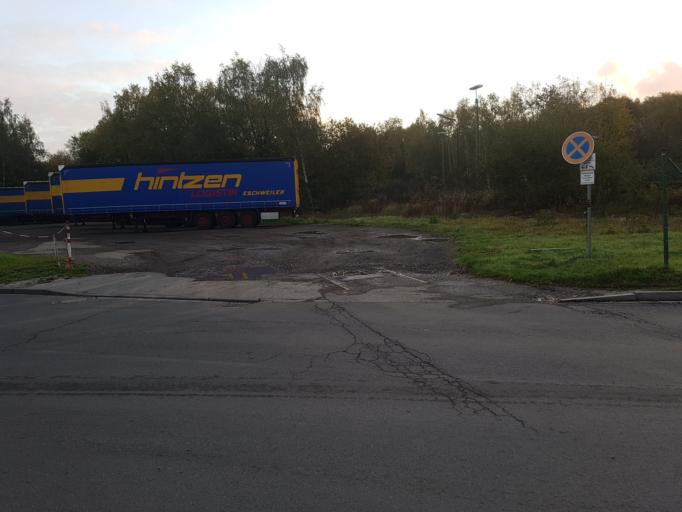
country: DE
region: North Rhine-Westphalia
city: Stolberg
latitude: 50.8053
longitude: 6.2388
